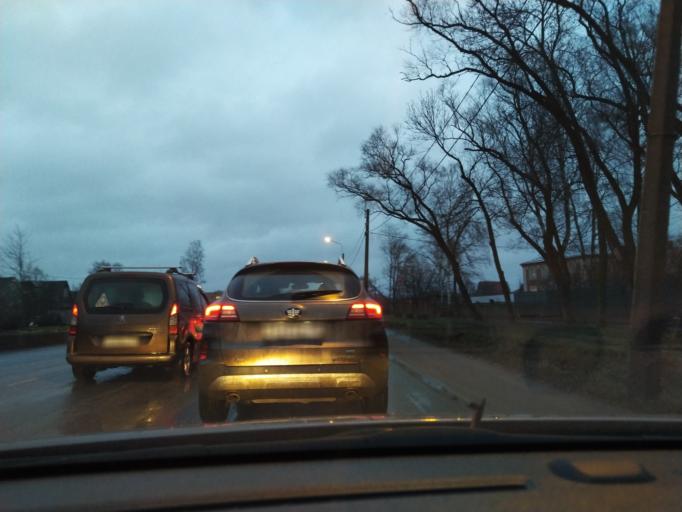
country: RU
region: St.-Petersburg
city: Uritsk
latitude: 59.8161
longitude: 30.1760
